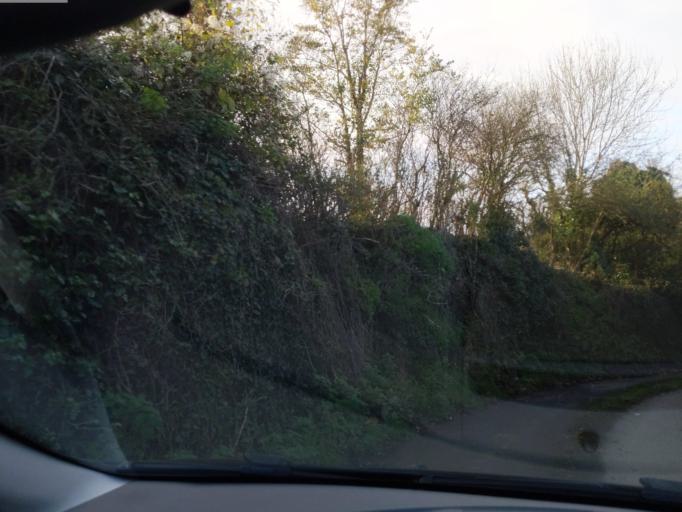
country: GB
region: England
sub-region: Cornwall
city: Wadebridge
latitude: 50.5072
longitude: -4.8019
